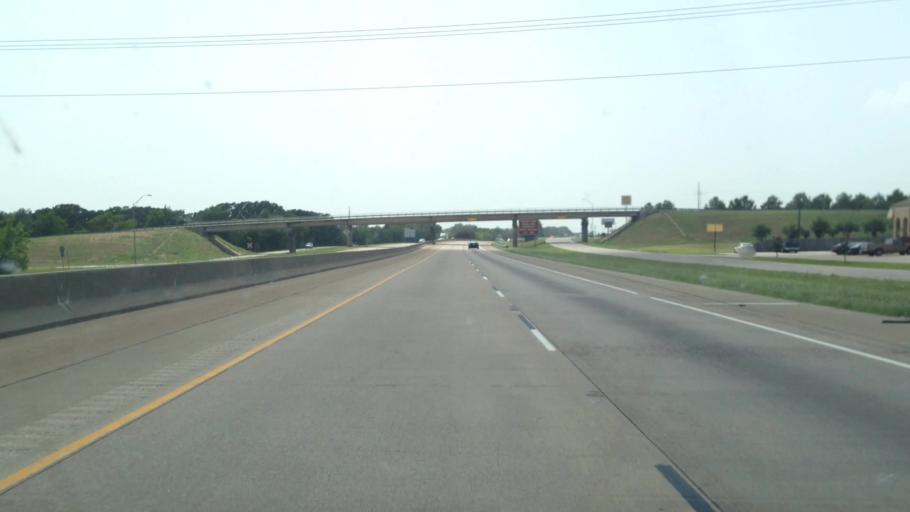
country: US
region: Texas
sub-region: Hopkins County
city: Sulphur Springs
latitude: 33.1164
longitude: -95.6100
